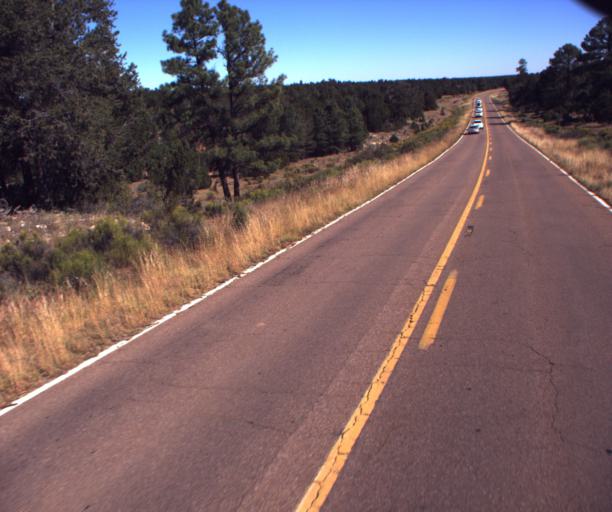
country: US
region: Arizona
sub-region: Navajo County
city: Heber-Overgaard
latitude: 34.4414
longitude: -110.5324
